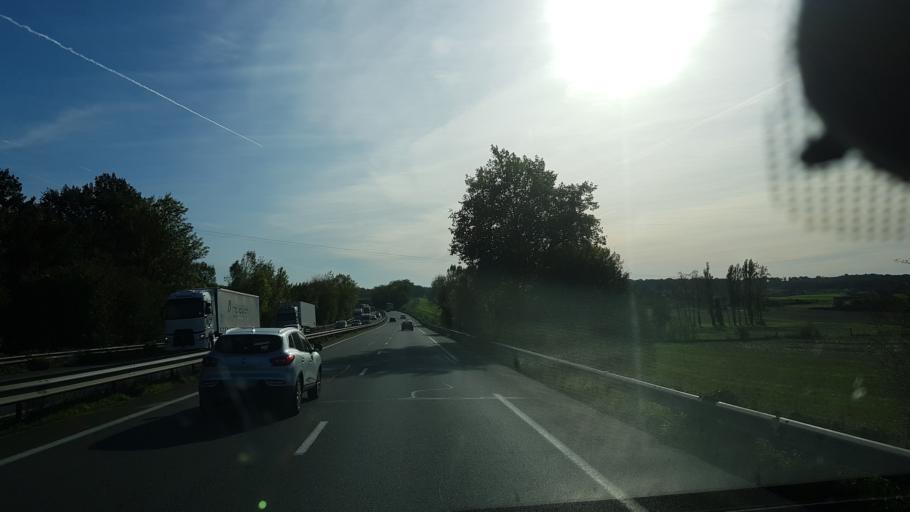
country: FR
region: Poitou-Charentes
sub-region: Departement de la Charente-Maritime
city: Chevanceaux
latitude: 45.3071
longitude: -0.2360
